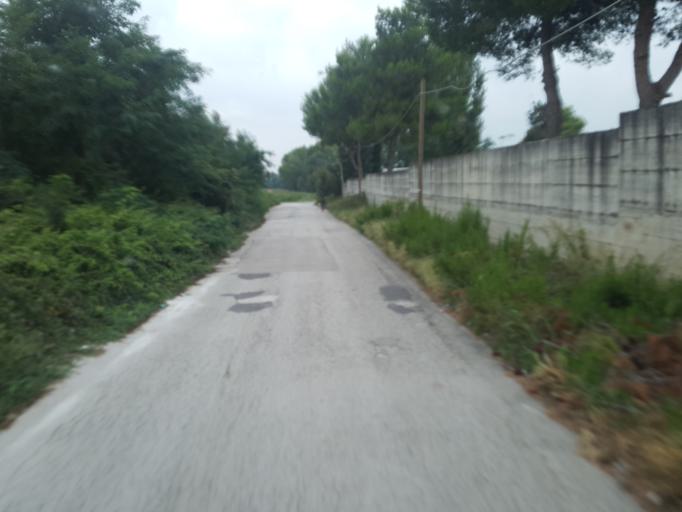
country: IT
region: Campania
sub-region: Provincia di Caserta
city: Pignataro Maggiore
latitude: 41.1687
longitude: 14.1545
